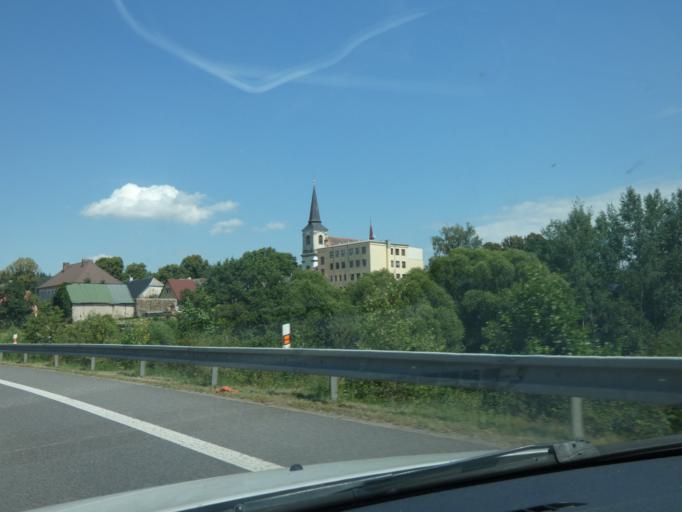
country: CZ
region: Pardubicky
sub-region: Okres Chrudim
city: Nasavrky
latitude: 49.7846
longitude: 15.8164
